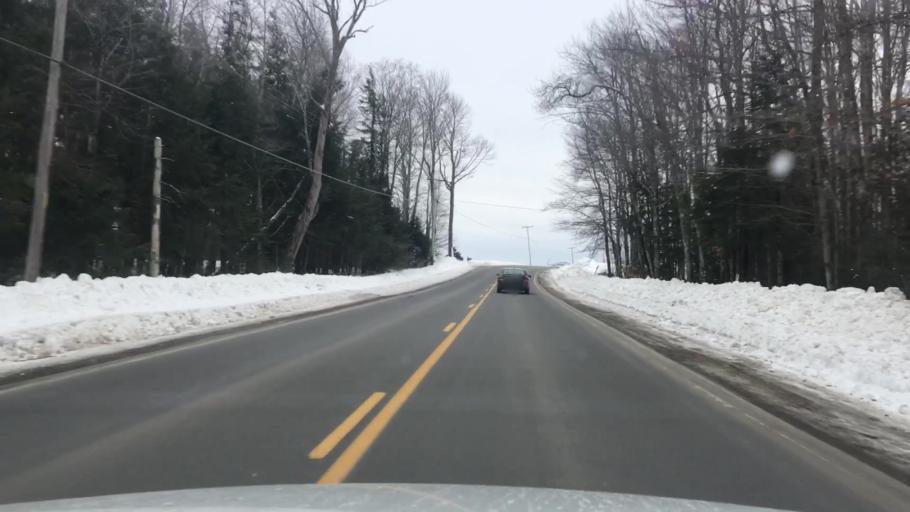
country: US
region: Maine
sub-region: Penobscot County
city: Garland
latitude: 44.9839
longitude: -69.0878
